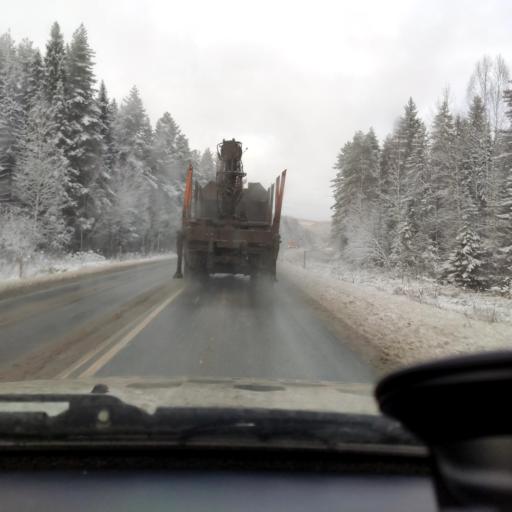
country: RU
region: Perm
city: Nytva
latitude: 57.9727
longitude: 55.3646
